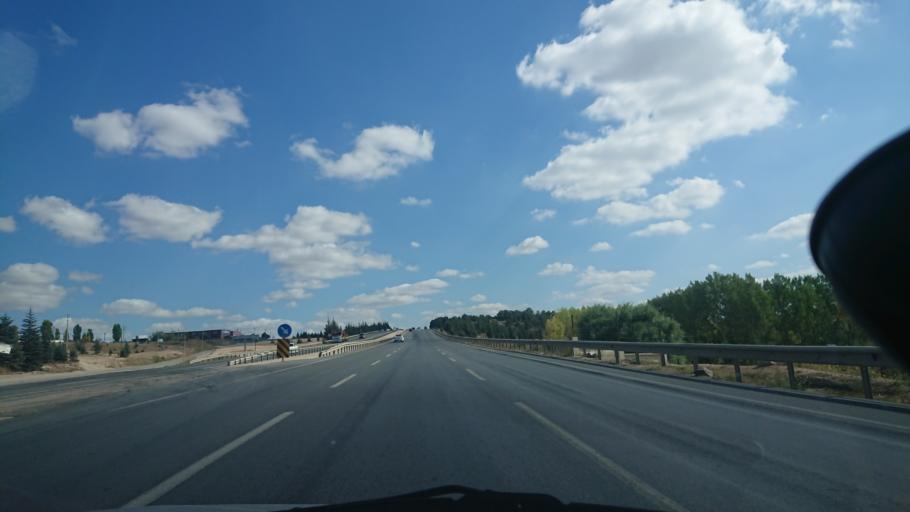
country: TR
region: Eskisehir
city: Sevinc
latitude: 39.7250
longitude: 30.6674
